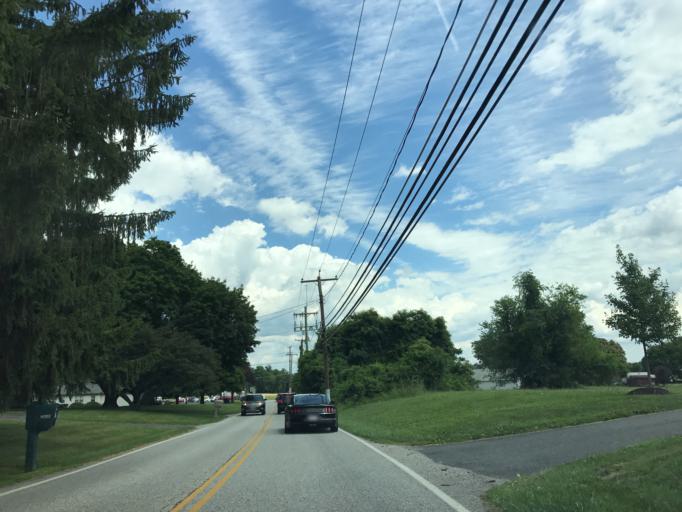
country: US
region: Maryland
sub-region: Harford County
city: Jarrettsville
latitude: 39.6008
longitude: -76.4840
